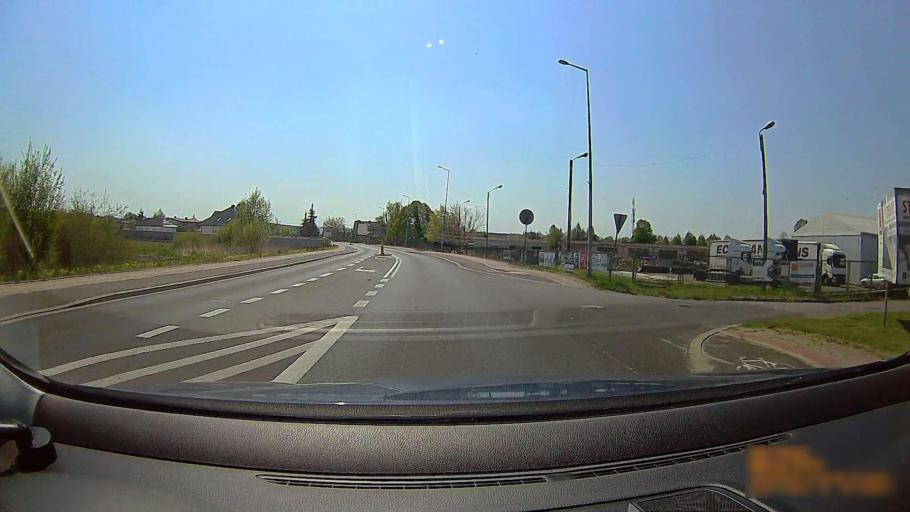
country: PL
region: Greater Poland Voivodeship
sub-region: Konin
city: Konin
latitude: 52.1968
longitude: 18.2613
